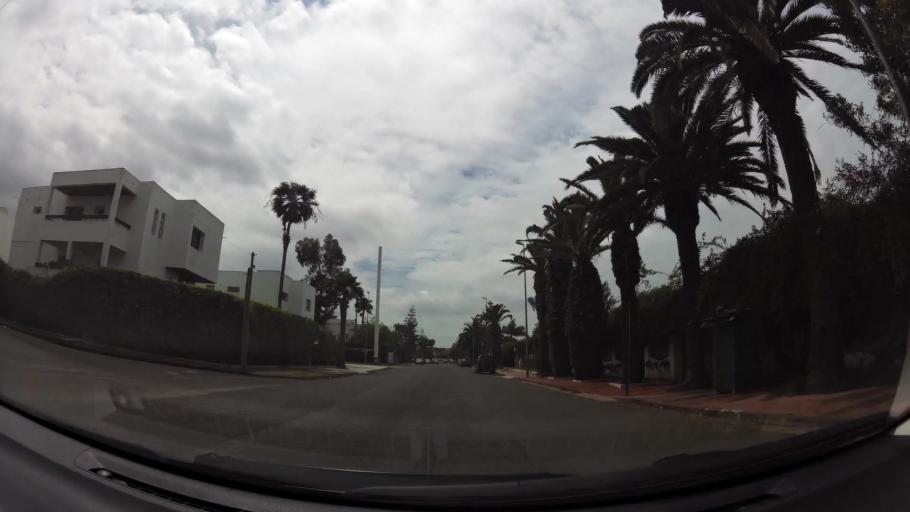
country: MA
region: Grand Casablanca
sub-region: Casablanca
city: Casablanca
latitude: 33.5732
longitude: -7.6624
